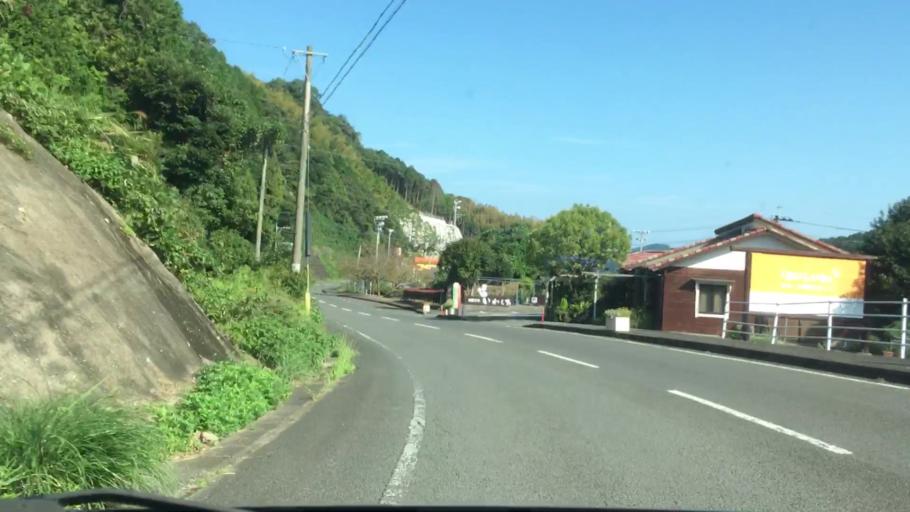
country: JP
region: Nagasaki
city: Sasebo
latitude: 32.9912
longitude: 129.6517
